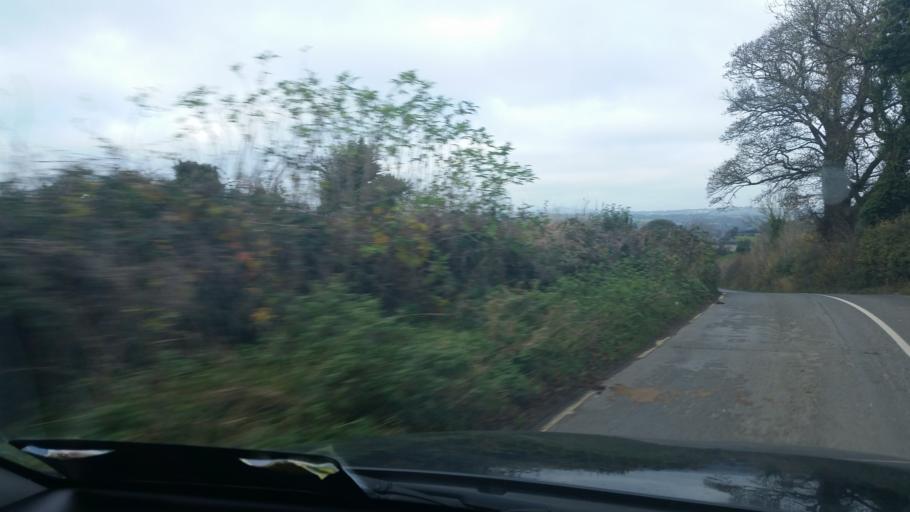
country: IE
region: Leinster
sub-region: Lu
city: Tullyallen
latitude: 53.7055
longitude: -6.4082
